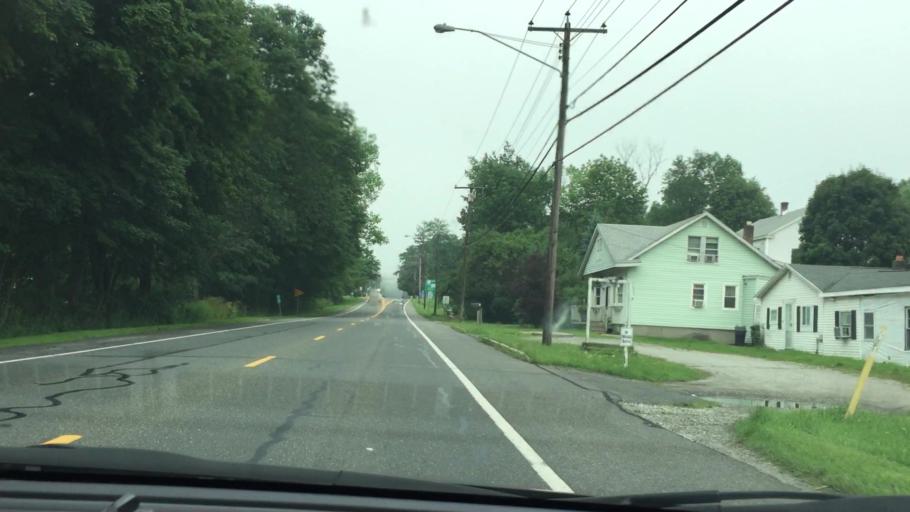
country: US
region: Massachusetts
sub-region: Berkshire County
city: Richmond
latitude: 42.4315
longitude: -73.3286
